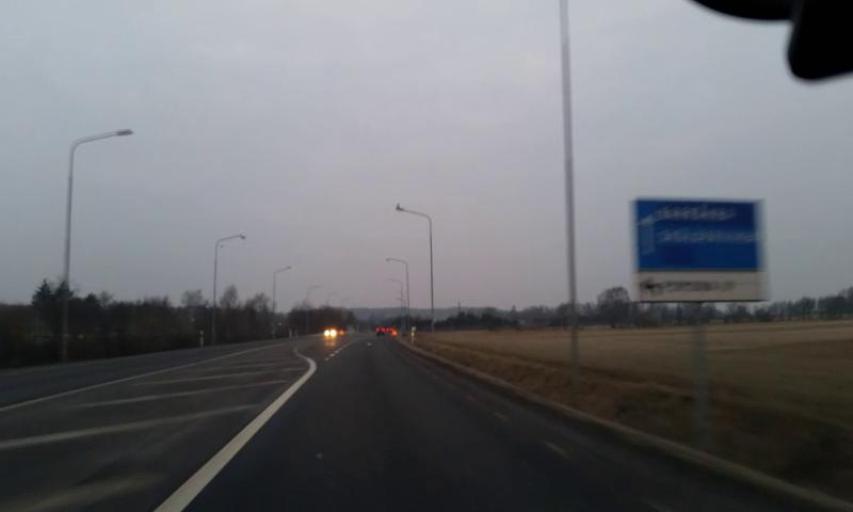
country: SE
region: Skane
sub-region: Angelholms Kommun
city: AEngelholm
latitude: 56.2721
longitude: 12.8577
